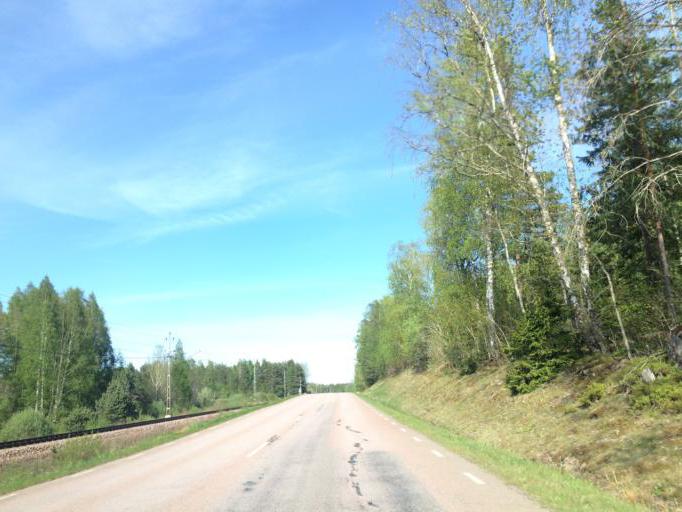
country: SE
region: Soedermanland
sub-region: Eskilstuna Kommun
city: Kvicksund
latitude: 59.4179
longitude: 16.2833
